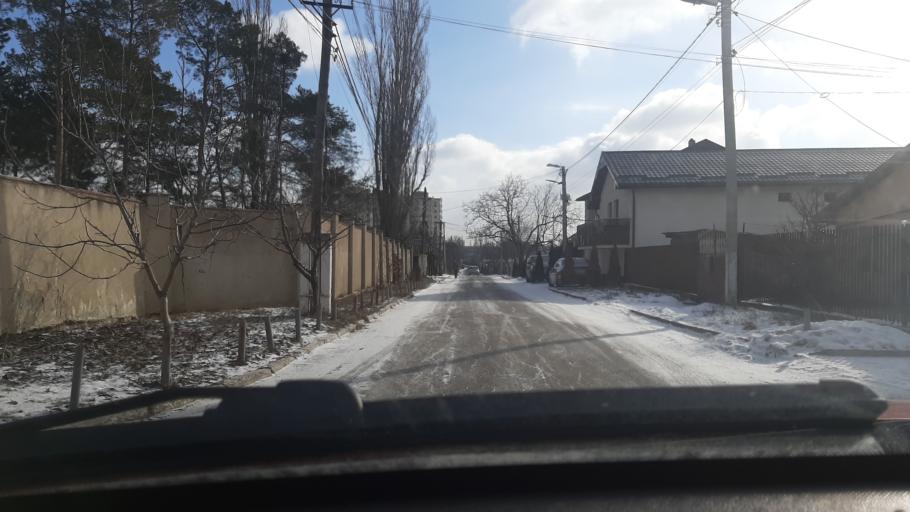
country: MD
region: Laloveni
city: Ialoveni
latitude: 46.9928
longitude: 28.7799
